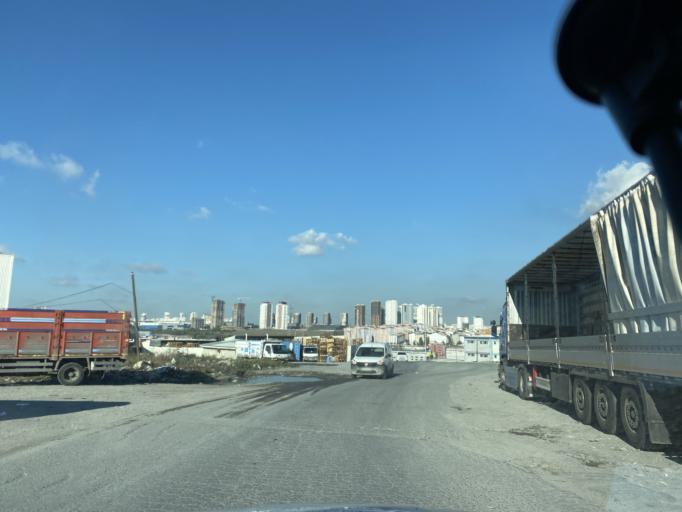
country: TR
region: Istanbul
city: Esenyurt
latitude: 41.0553
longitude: 28.6481
